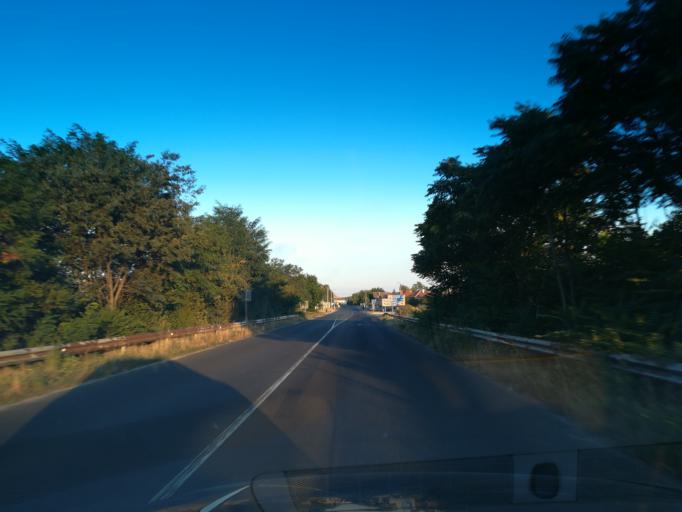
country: BG
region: Plovdiv
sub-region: Obshtina Sadovo
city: Sadovo
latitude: 42.1380
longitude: 25.0508
